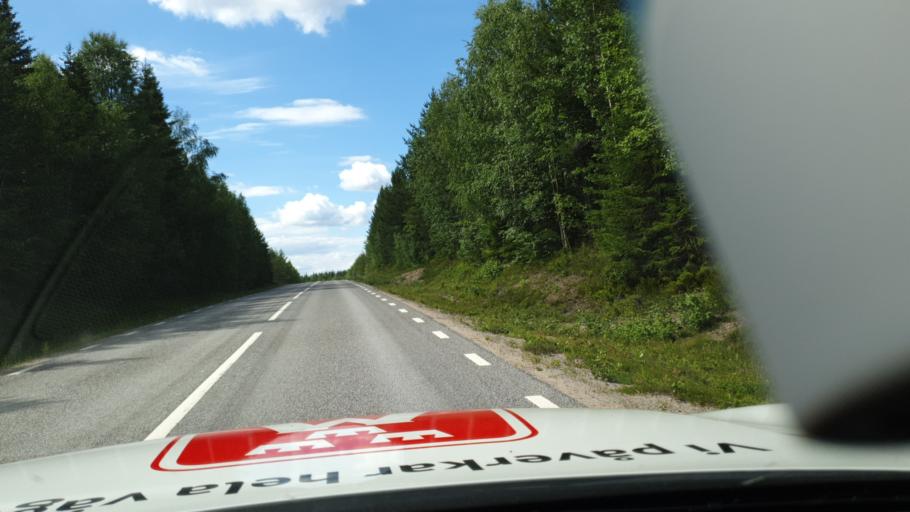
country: SE
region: Jaemtland
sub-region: Harjedalens Kommun
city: Sveg
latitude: 61.9988
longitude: 14.9552
